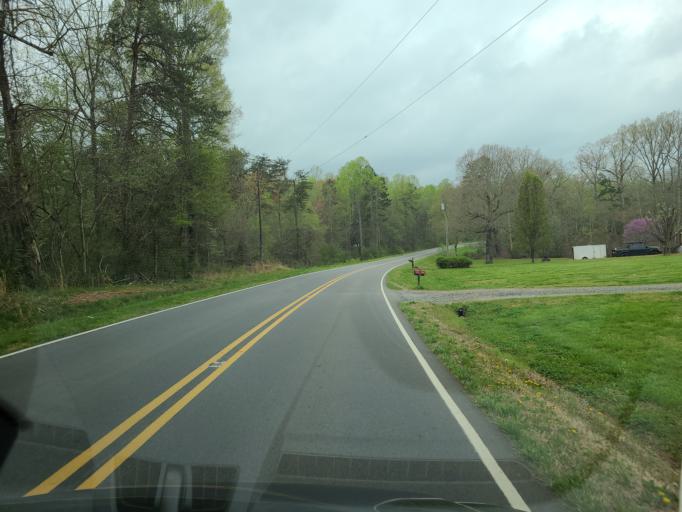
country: US
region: North Carolina
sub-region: Gaston County
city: Cherryville
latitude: 35.4366
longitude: -81.4090
